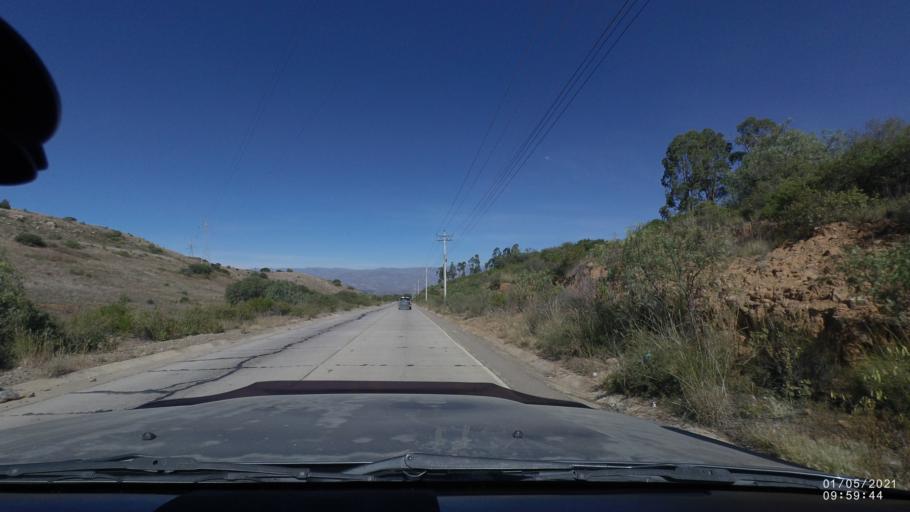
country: BO
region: Cochabamba
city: Cochabamba
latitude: -17.5273
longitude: -66.1913
